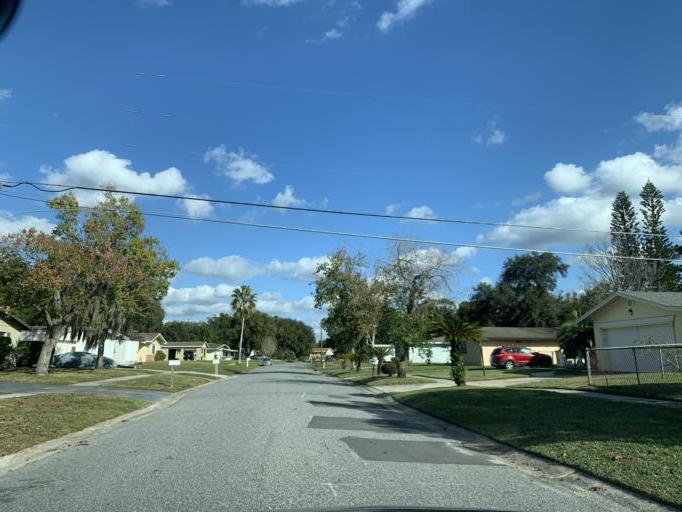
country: US
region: Florida
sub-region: Orange County
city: Fairview Shores
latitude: 28.6118
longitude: -81.4031
